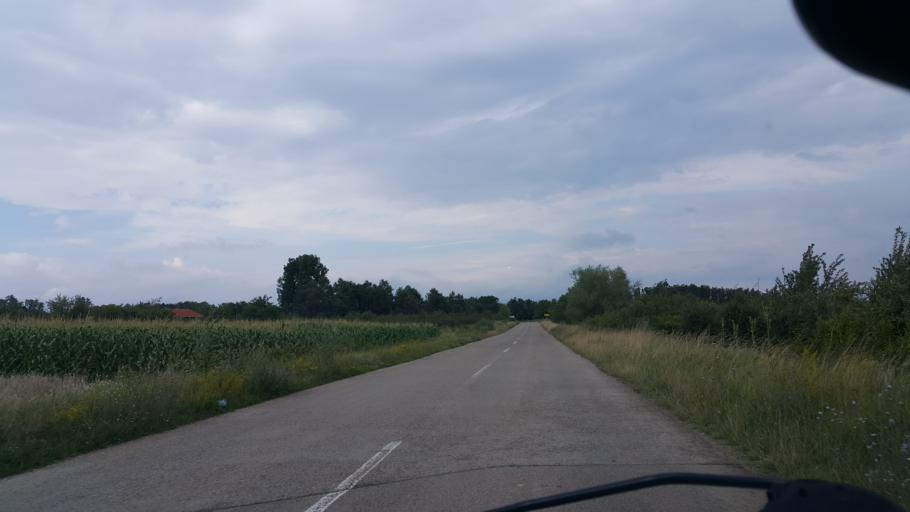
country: RS
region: Central Serbia
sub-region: Toplicki Okrug
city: Blace
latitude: 43.2506
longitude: 21.2617
